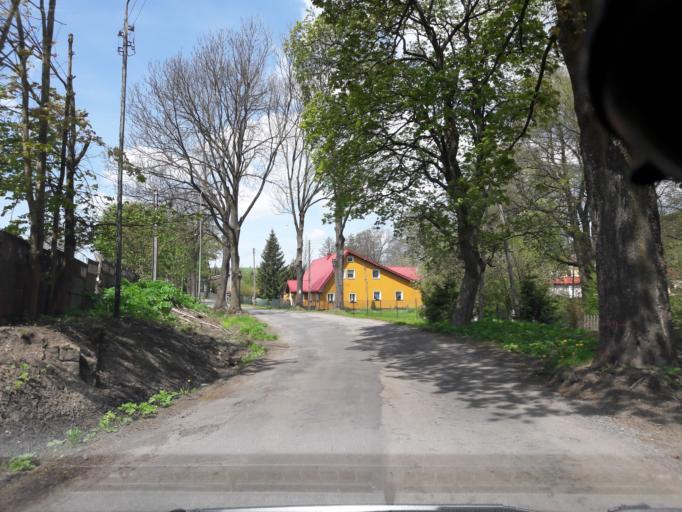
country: PL
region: Lower Silesian Voivodeship
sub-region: Powiat klodzki
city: Duszniki-Zdroj
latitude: 50.4269
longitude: 16.3696
